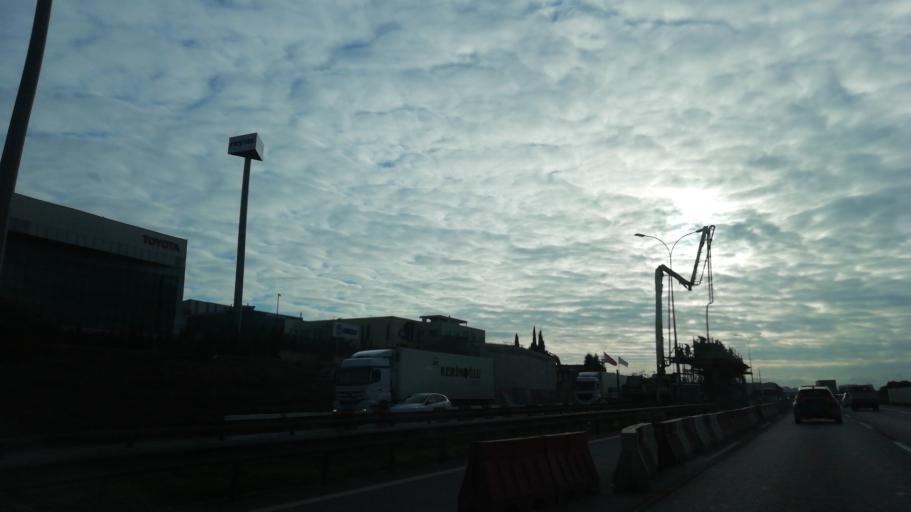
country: TR
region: Kocaeli
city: Balcik
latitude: 40.8835
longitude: 29.3779
